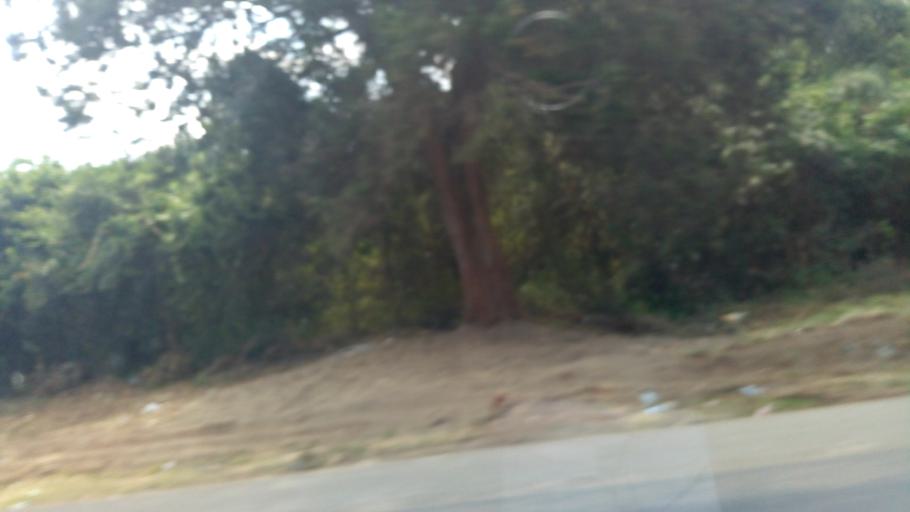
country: KE
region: Kiambu
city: Limuru
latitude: -1.0797
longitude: 36.6027
